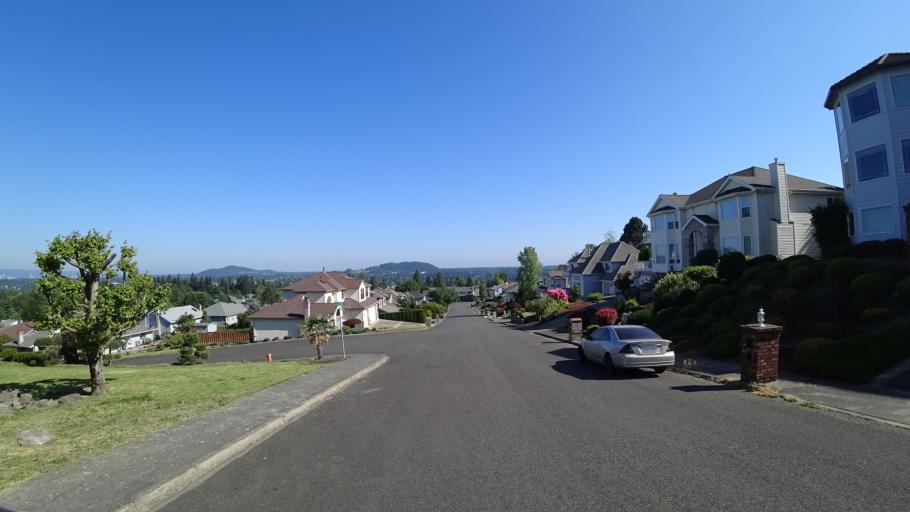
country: US
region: Oregon
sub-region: Multnomah County
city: Lents
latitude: 45.4666
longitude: -122.5493
